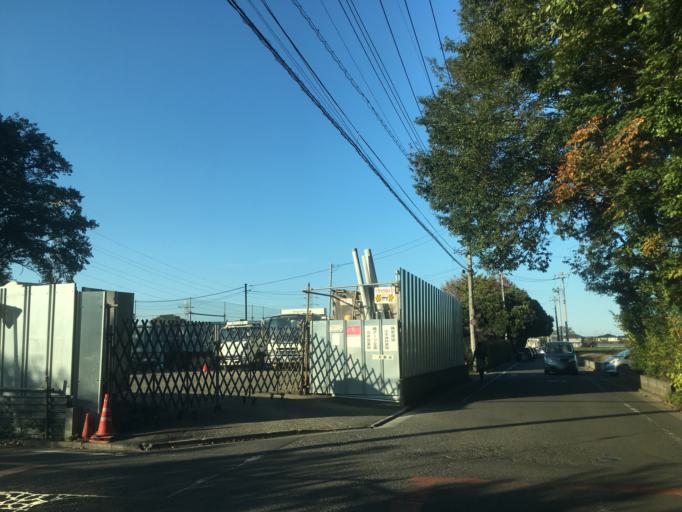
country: JP
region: Saitama
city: Tokorozawa
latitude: 35.8152
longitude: 139.4397
